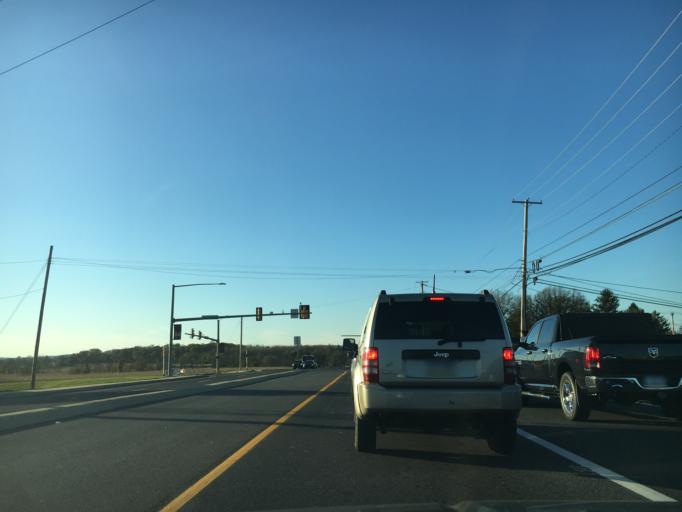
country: US
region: Pennsylvania
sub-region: Lehigh County
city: Stiles
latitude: 40.6521
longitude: -75.5024
